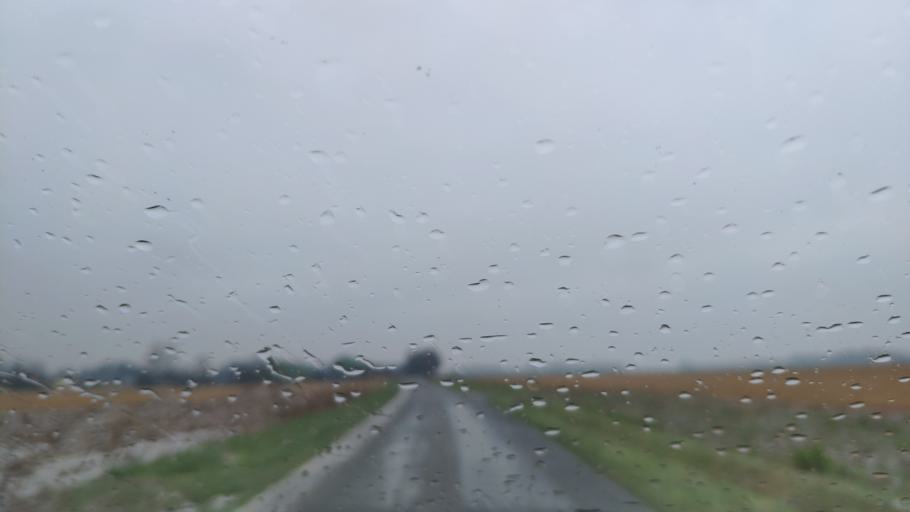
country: FR
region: Haute-Normandie
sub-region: Departement de la Seine-Maritime
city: Cany-Barville
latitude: 49.7930
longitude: 0.6718
